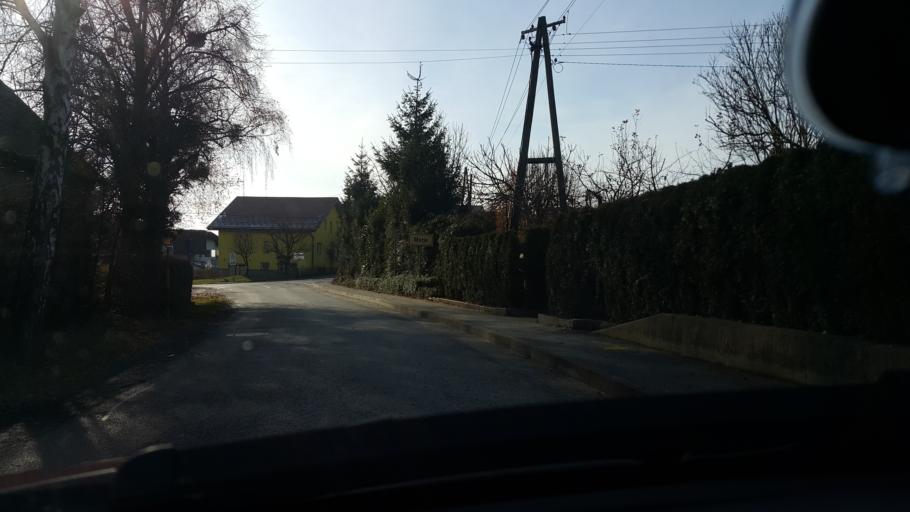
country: SI
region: Race-Fram
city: Fram
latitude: 46.4508
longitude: 15.6361
